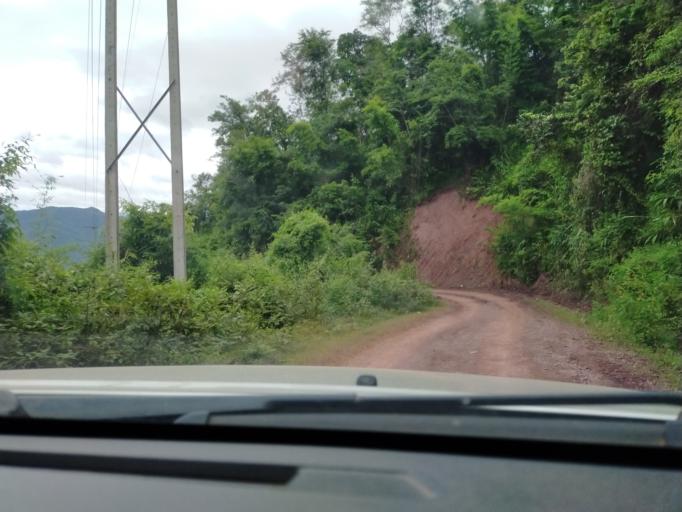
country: TH
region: Nan
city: Chaloem Phra Kiat
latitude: 19.7787
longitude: 101.3586
